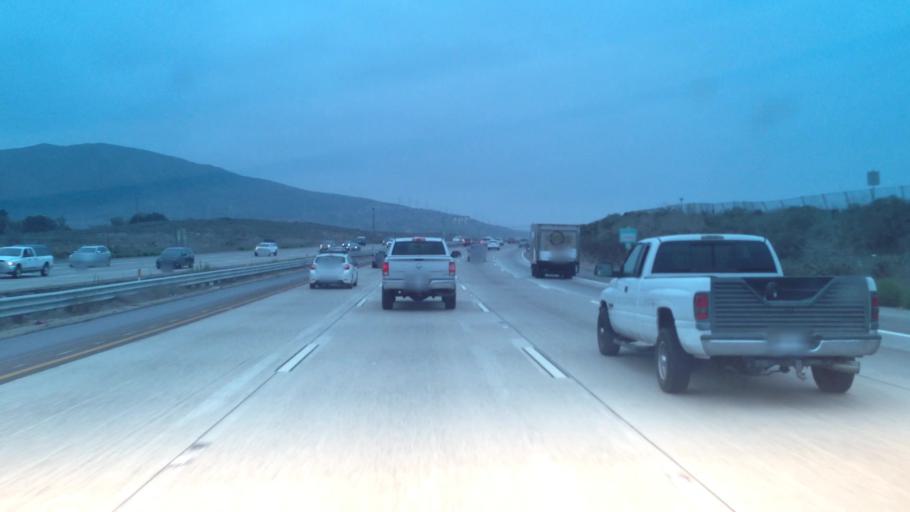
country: US
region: California
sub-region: Orange County
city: San Clemente
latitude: 33.3792
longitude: -117.5673
